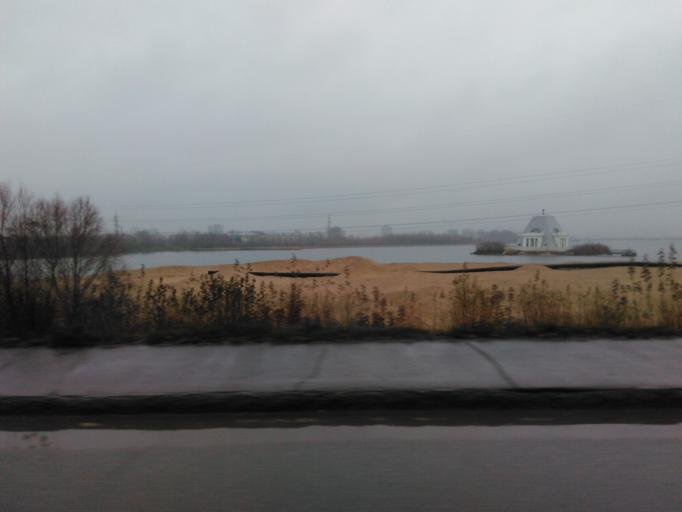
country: RU
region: Tatarstan
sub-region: Gorod Kazan'
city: Kazan
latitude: 55.7995
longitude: 49.0734
